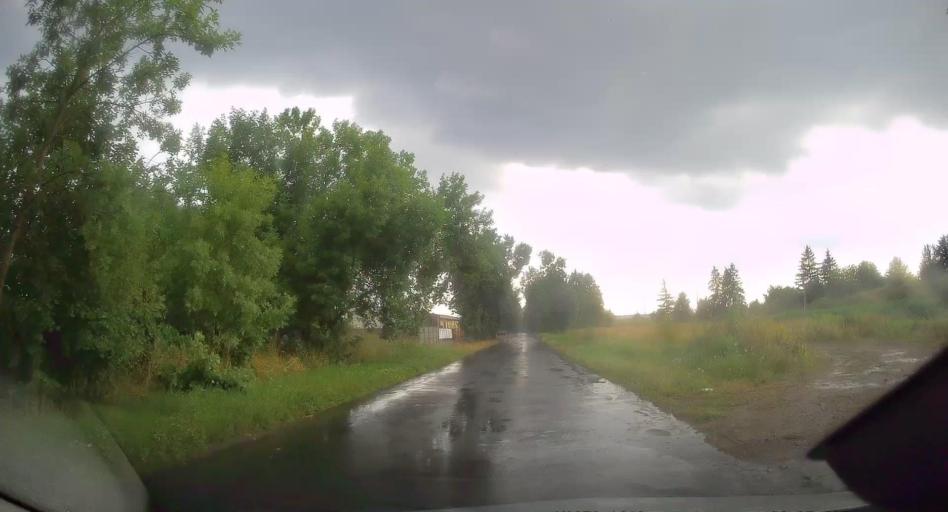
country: PL
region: Lodz Voivodeship
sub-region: Powiat brzezinski
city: Rogow
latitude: 51.8108
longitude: 19.8767
